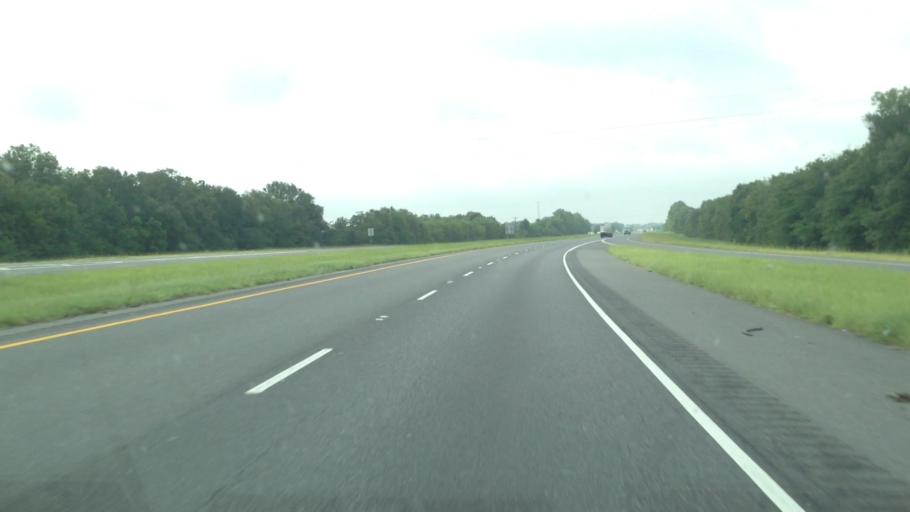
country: US
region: Louisiana
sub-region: Saint Landry Parish
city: Opelousas
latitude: 30.6389
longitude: -92.0486
